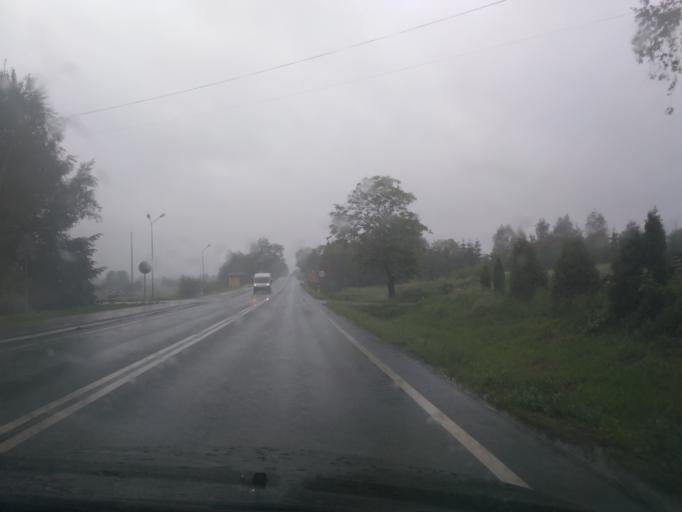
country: PL
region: Subcarpathian Voivodeship
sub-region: Powiat jasielski
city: Tarnowiec
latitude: 49.7628
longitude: 21.5631
